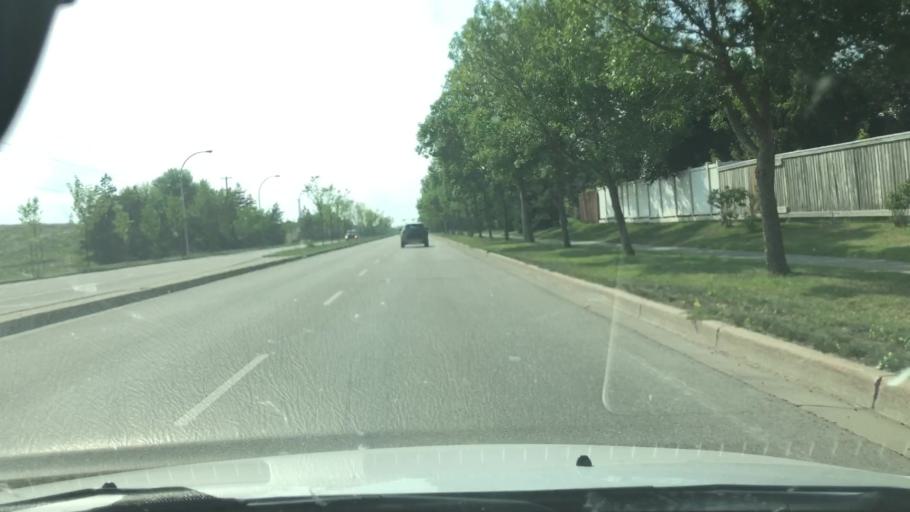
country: CA
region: Alberta
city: Edmonton
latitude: 53.6142
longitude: -113.5034
